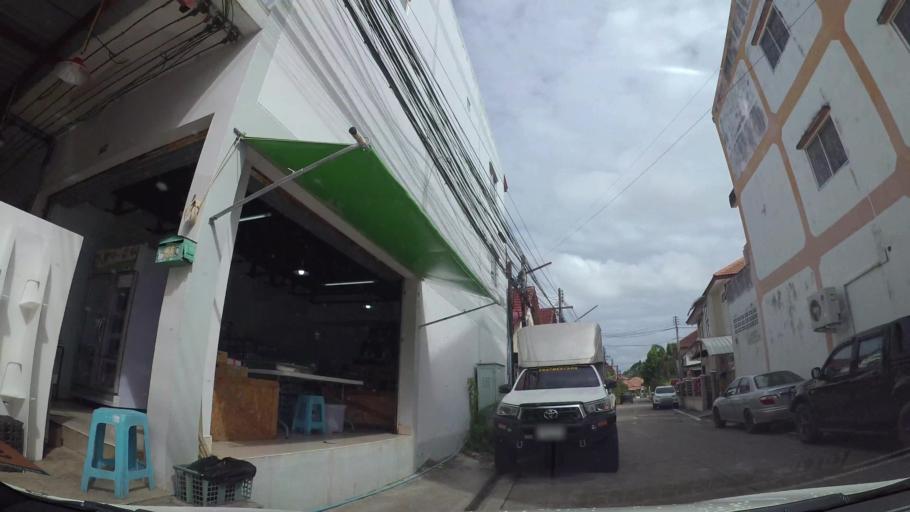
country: TH
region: Rayong
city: Rayong
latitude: 12.6691
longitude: 101.2888
